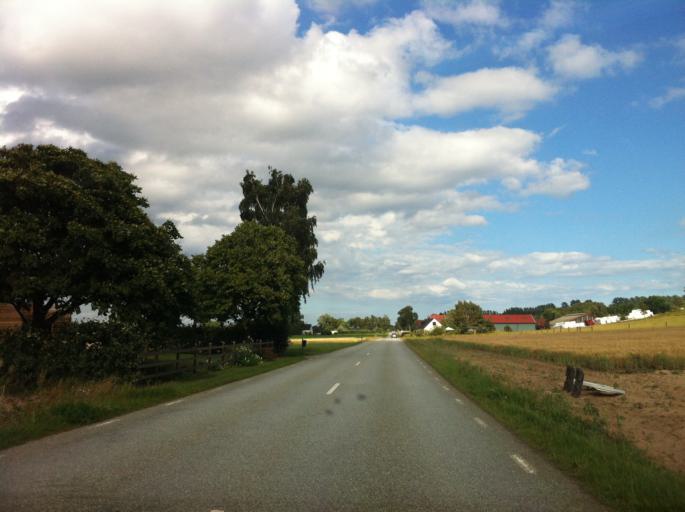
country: SE
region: Skane
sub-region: Ystads Kommun
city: Kopingebro
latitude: 55.3945
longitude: 14.1393
